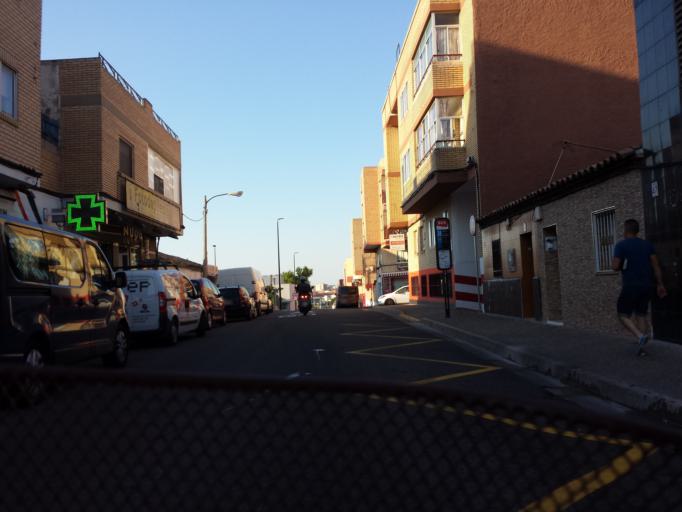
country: ES
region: Aragon
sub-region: Provincia de Zaragoza
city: Oliver-Valdefierro, Oliver, Valdefierro
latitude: 41.6404
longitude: -0.9291
